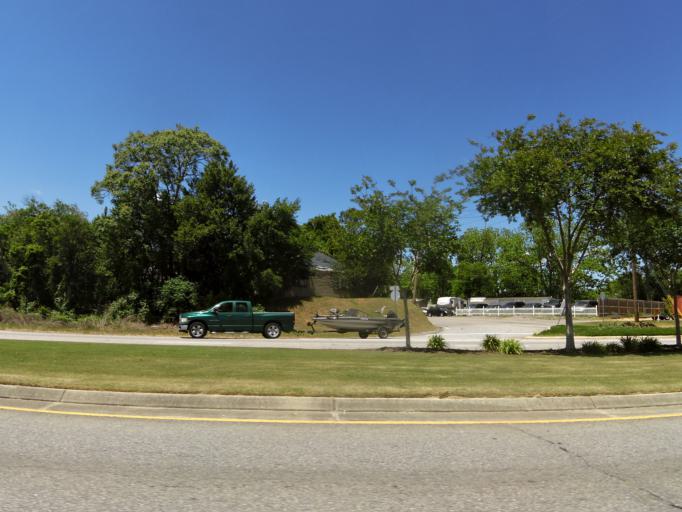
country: US
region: South Carolina
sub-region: Aiken County
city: North Augusta
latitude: 33.4841
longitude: -81.9463
